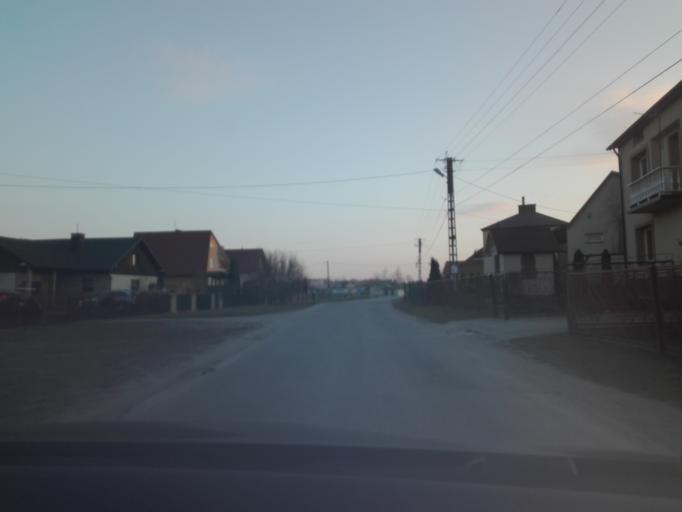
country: PL
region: Subcarpathian Voivodeship
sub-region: Powiat tarnobrzeski
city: Sokolniki
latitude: 50.6471
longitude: 21.8011
